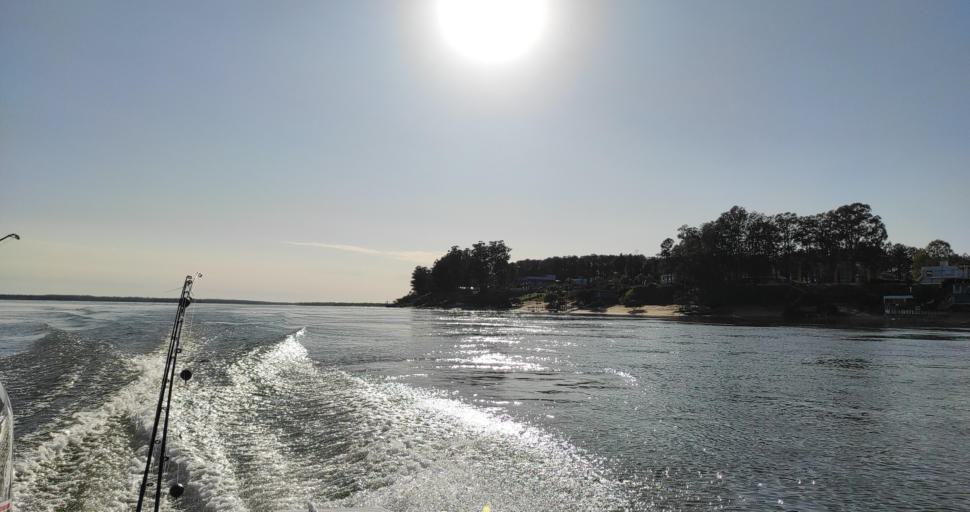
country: AR
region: Corrientes
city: Ituzaingo
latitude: -27.5994
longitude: -56.8172
